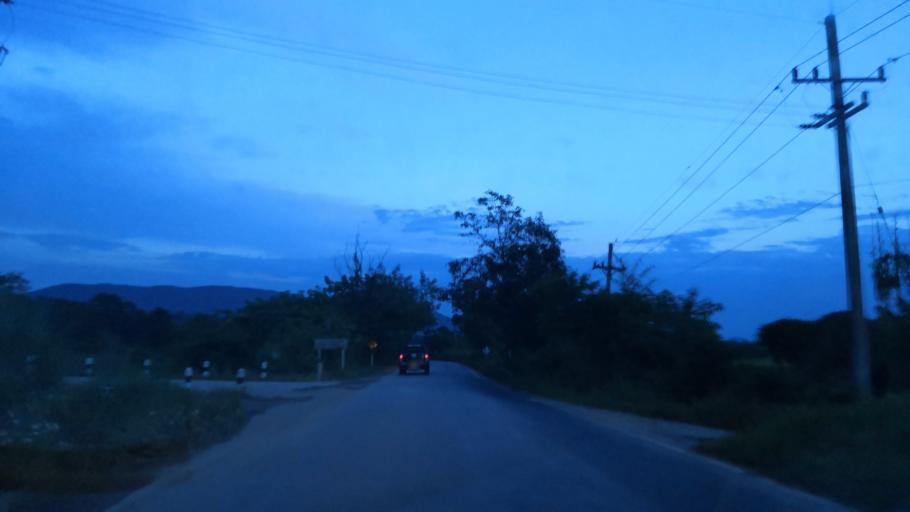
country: TH
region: Chiang Rai
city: Wiang Chiang Rung
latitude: 19.9659
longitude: 99.9835
